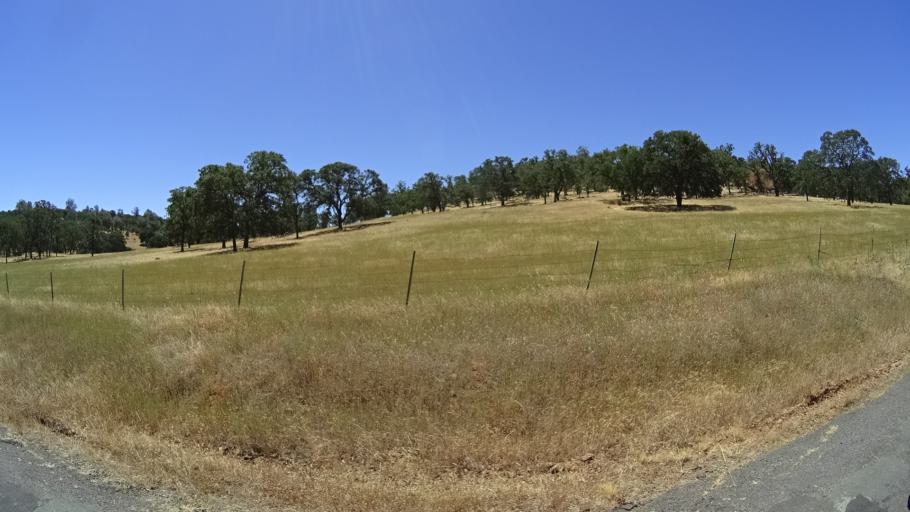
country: US
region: California
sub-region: Calaveras County
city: Rancho Calaveras
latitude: 38.0493
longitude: -120.7878
